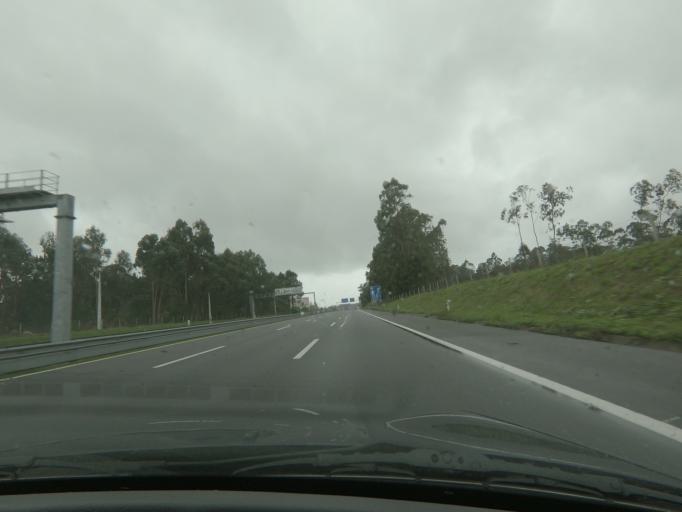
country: PT
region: Porto
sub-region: Matosinhos
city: Santa Cruz do Bispo
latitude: 41.2322
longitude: -8.6881
